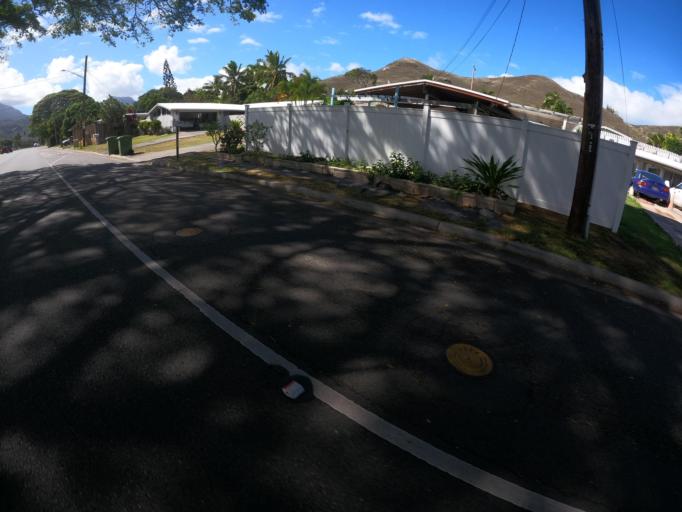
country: US
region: Hawaii
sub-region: Honolulu County
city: Kailua
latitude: 21.4107
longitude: -157.7543
